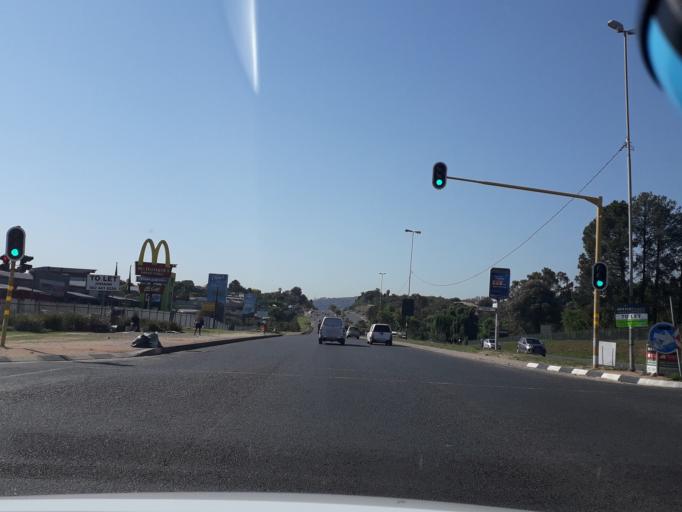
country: ZA
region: Gauteng
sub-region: City of Johannesburg Metropolitan Municipality
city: Roodepoort
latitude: -26.0929
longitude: 27.9393
